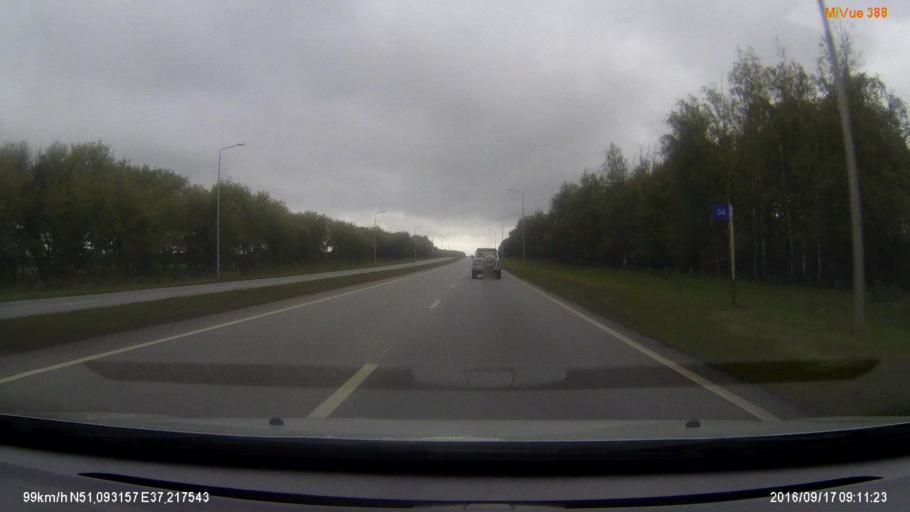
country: RU
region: Belgorod
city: Skorodnoye
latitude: 51.0927
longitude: 37.2173
